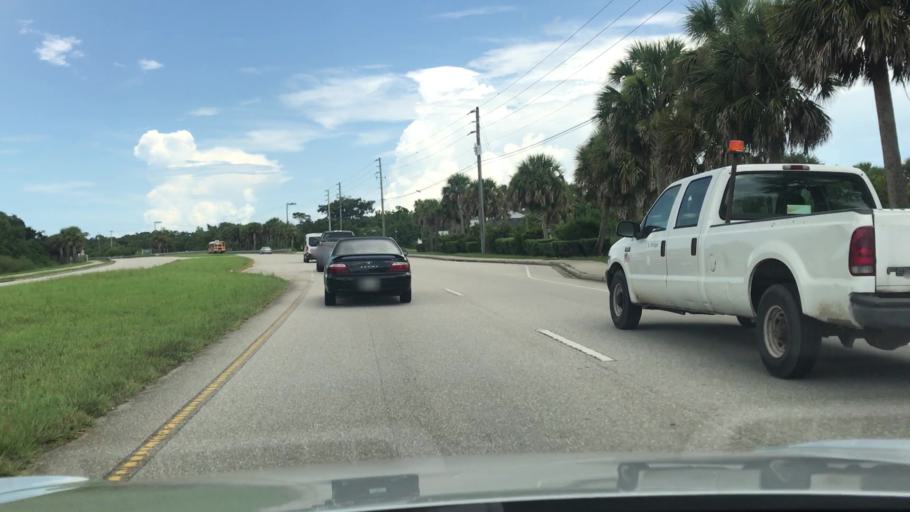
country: US
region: Florida
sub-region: Indian River County
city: Sebastian
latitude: 27.7677
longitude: -80.5080
